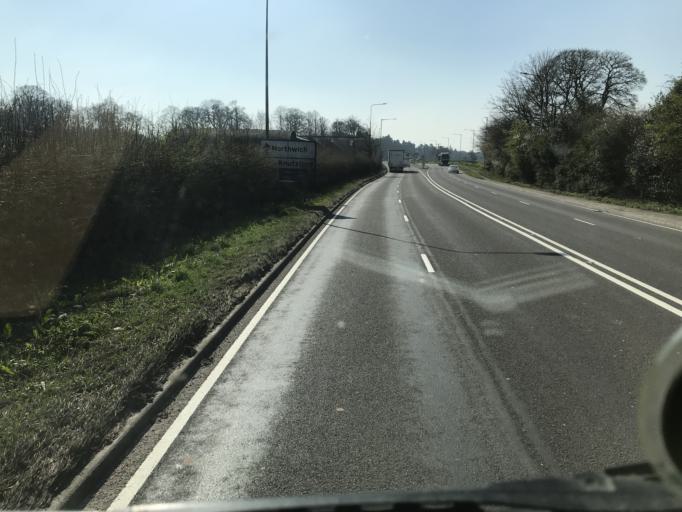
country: GB
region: England
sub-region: Cheshire East
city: Mere
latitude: 53.3034
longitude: -2.4188
